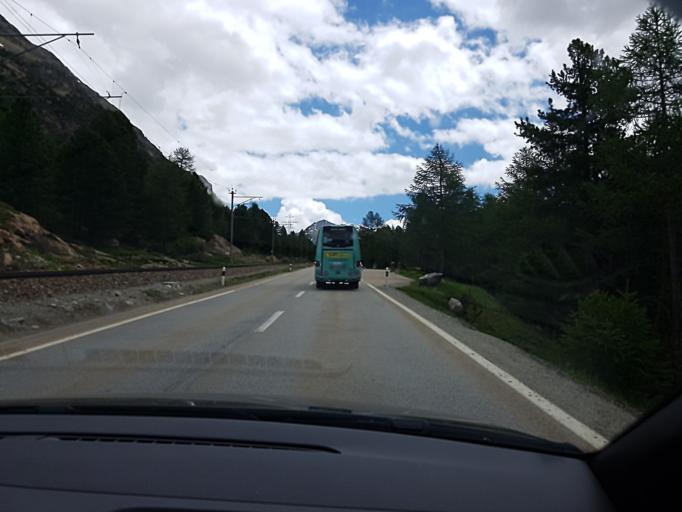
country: CH
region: Grisons
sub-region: Maloja District
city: Pontresina
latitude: 46.4536
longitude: 9.9470
